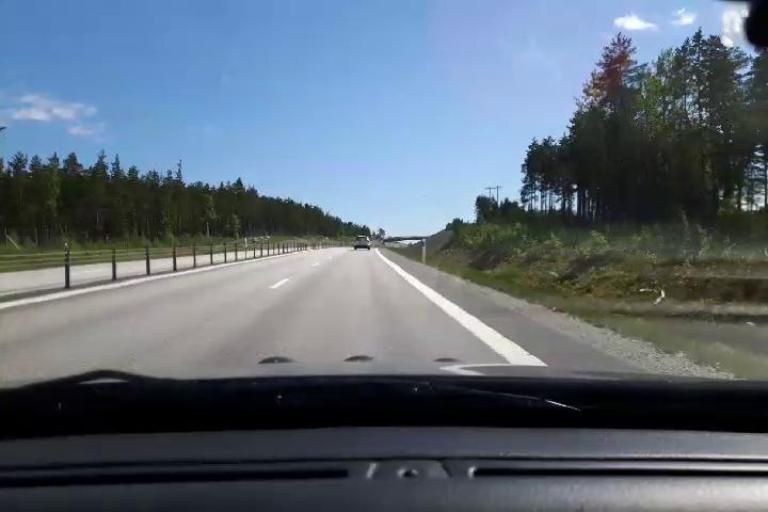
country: SE
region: Gaevleborg
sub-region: Hudiksvalls Kommun
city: Hudiksvall
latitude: 61.6969
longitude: 17.0568
